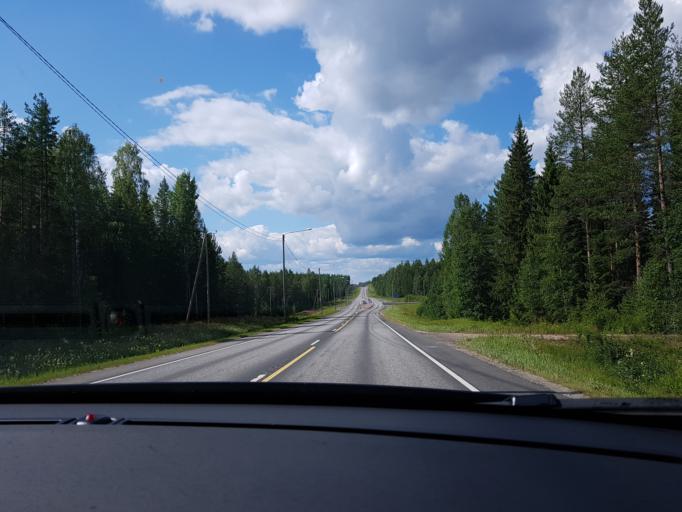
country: FI
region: Kainuu
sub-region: Kajaani
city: Ristijaervi
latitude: 64.3260
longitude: 28.0648
